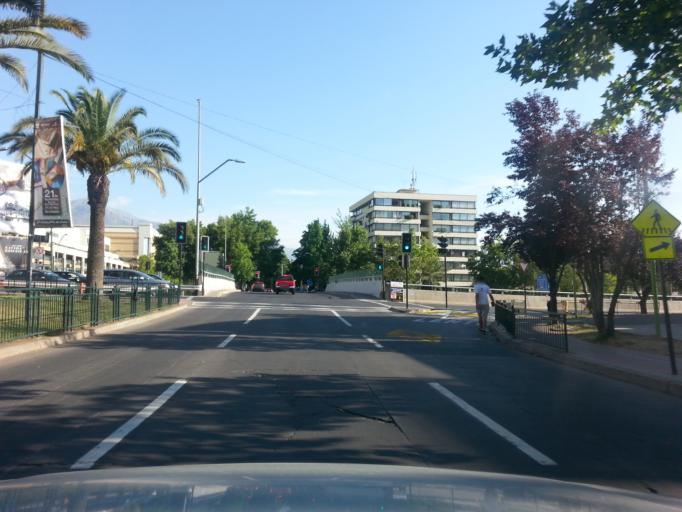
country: CL
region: Santiago Metropolitan
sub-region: Provincia de Santiago
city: Villa Presidente Frei, Nunoa, Santiago, Chile
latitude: -33.3892
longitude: -70.5486
